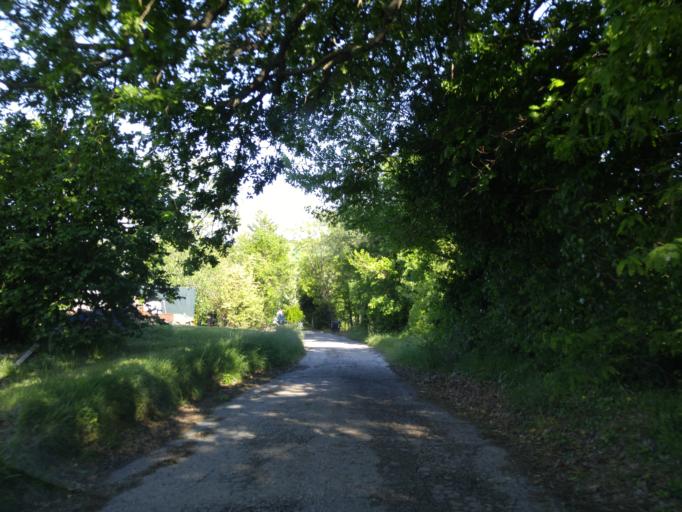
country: IT
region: The Marches
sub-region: Provincia di Pesaro e Urbino
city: Monteciccardo
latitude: 43.8233
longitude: 12.8362
